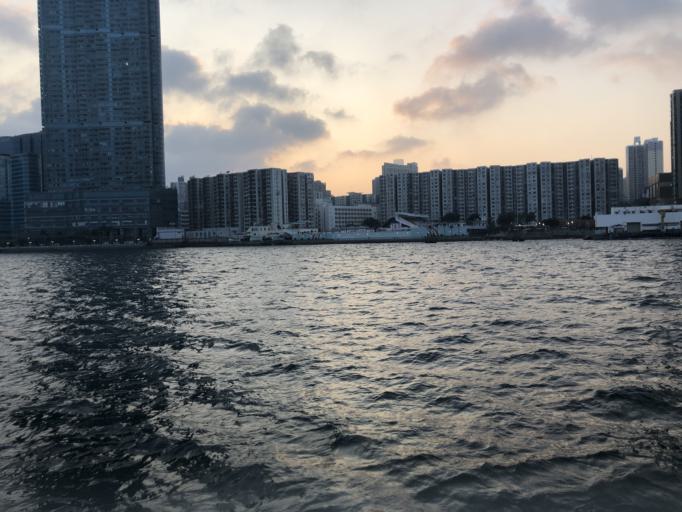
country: HK
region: Kowloon City
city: Kowloon
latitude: 22.3054
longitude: 114.1959
